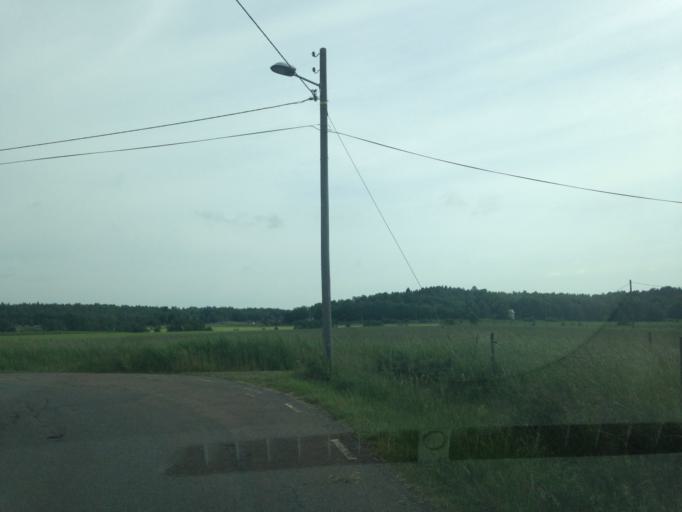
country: SE
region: Vaestra Goetaland
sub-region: Goteborg
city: Majorna
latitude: 57.7576
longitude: 11.8613
